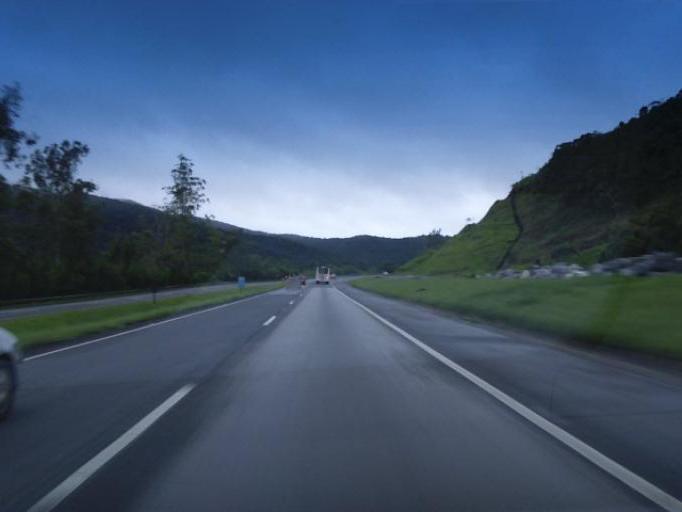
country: BR
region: Sao Paulo
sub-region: Miracatu
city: Miracatu
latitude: -24.1479
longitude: -47.3042
